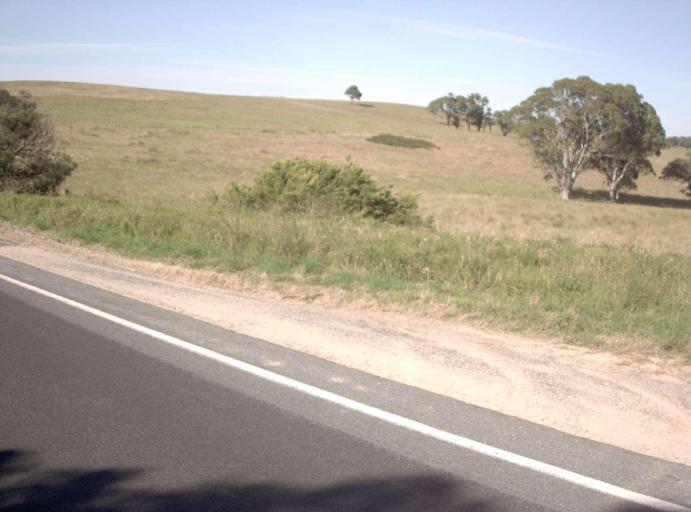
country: AU
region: Victoria
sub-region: East Gippsland
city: Lakes Entrance
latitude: -37.8652
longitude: 147.8471
